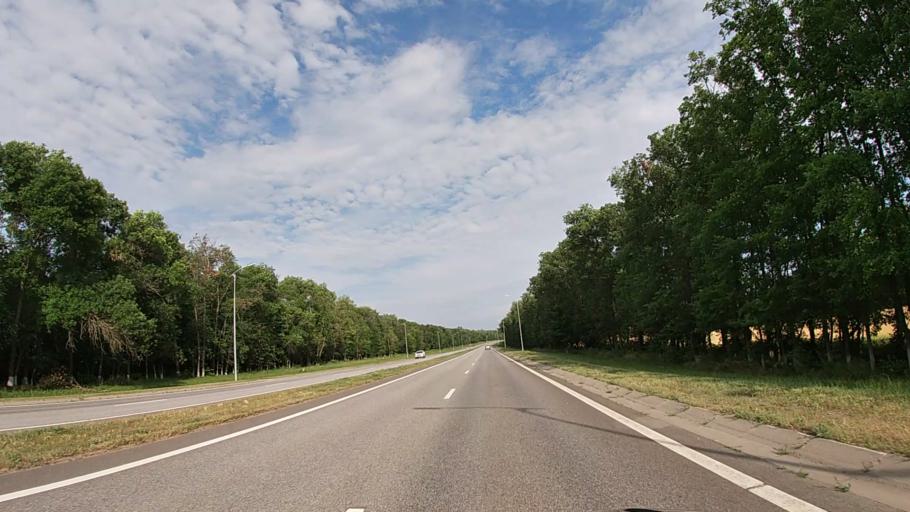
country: RU
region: Belgorod
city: Tomarovka
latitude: 50.6661
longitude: 36.3168
